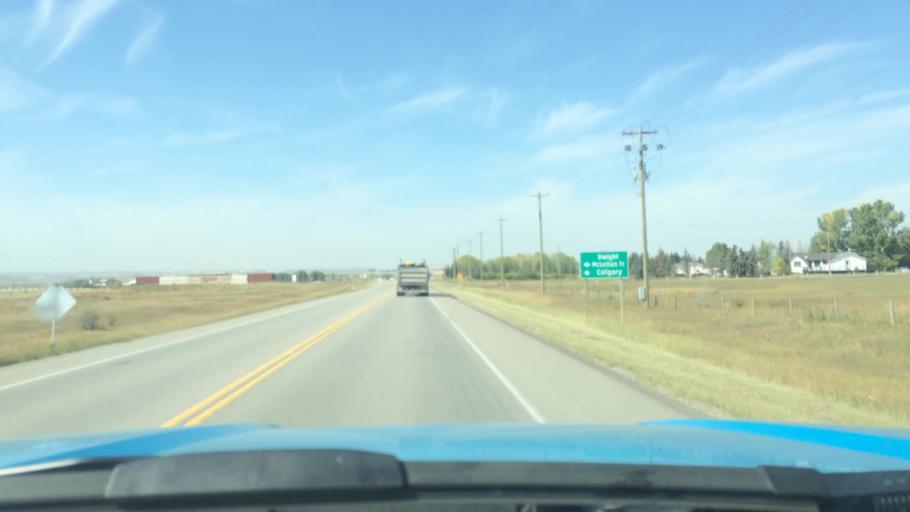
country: CA
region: Alberta
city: Airdrie
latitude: 51.2126
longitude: -113.9735
